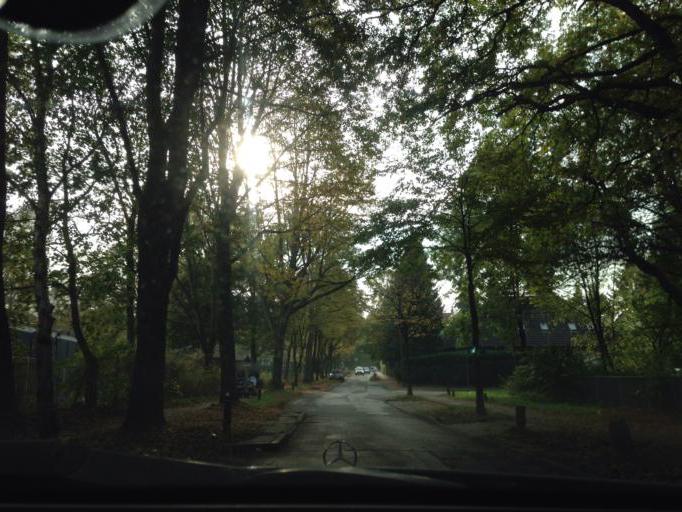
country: DE
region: Schleswig-Holstein
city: Barsbuettel
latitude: 53.5960
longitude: 10.1765
